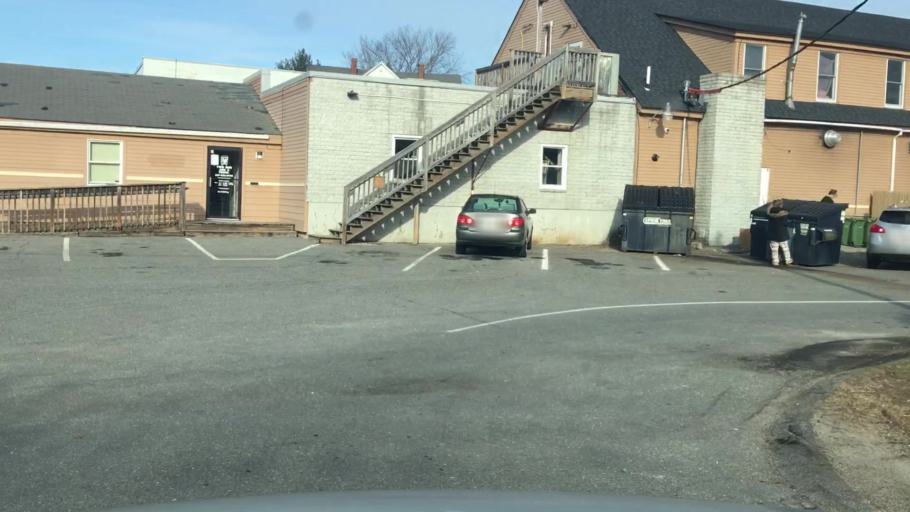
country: US
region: Maine
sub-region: Cumberland County
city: Westbrook
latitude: 43.7037
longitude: -70.3259
